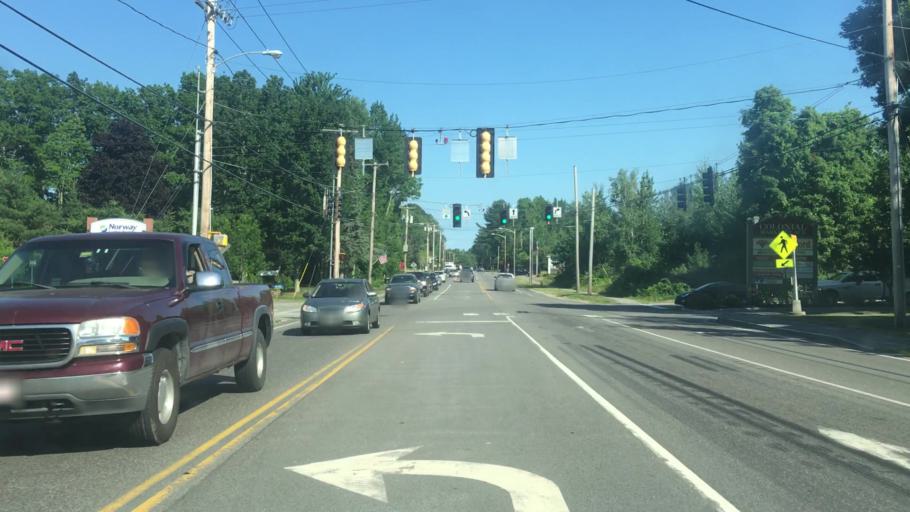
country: US
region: Maine
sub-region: York County
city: Buxton
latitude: 43.7320
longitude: -70.5439
